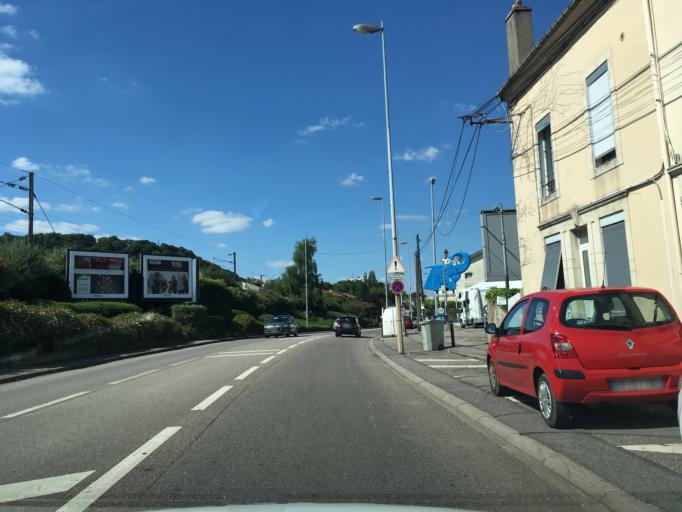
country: FR
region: Lorraine
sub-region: Departement de Meurthe-et-Moselle
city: Maxeville
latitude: 48.7152
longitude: 6.1686
